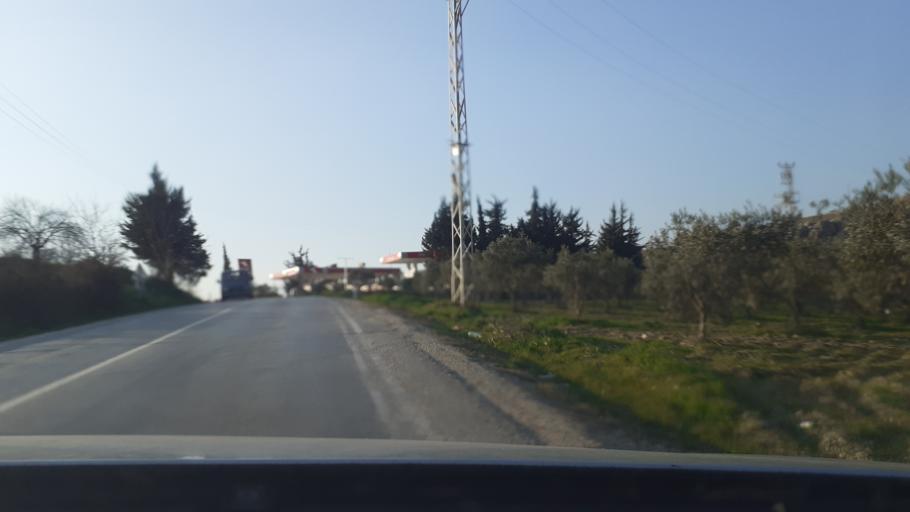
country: TR
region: Hatay
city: Fatikli
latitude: 36.1106
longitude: 36.2695
